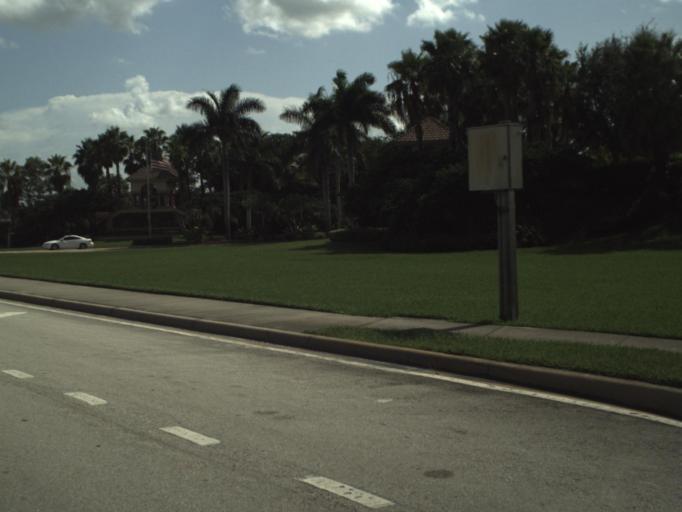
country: US
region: Florida
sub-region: Palm Beach County
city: Royal Palm Beach
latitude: 26.6888
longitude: -80.2020
